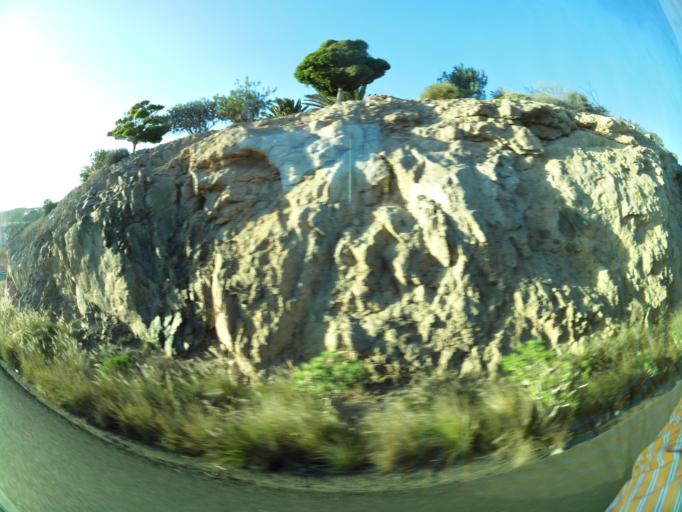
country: ES
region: Canary Islands
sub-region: Provincia de Las Palmas
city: Playa del Ingles
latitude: 27.7723
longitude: -15.5371
